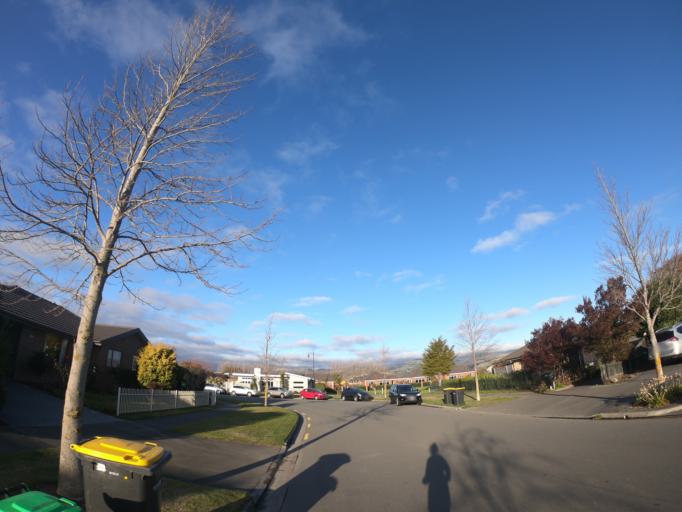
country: NZ
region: Canterbury
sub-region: Selwyn District
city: Prebbleton
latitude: -43.5681
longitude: 172.5698
